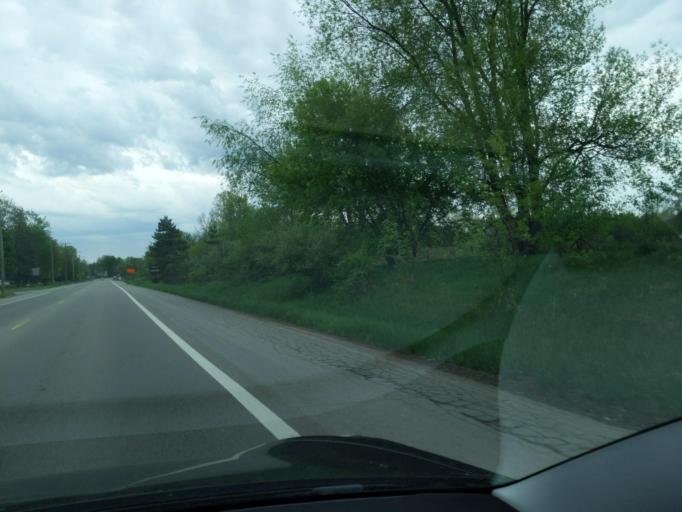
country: US
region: Michigan
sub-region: Washtenaw County
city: Chelsea
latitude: 42.3280
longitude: -84.0227
